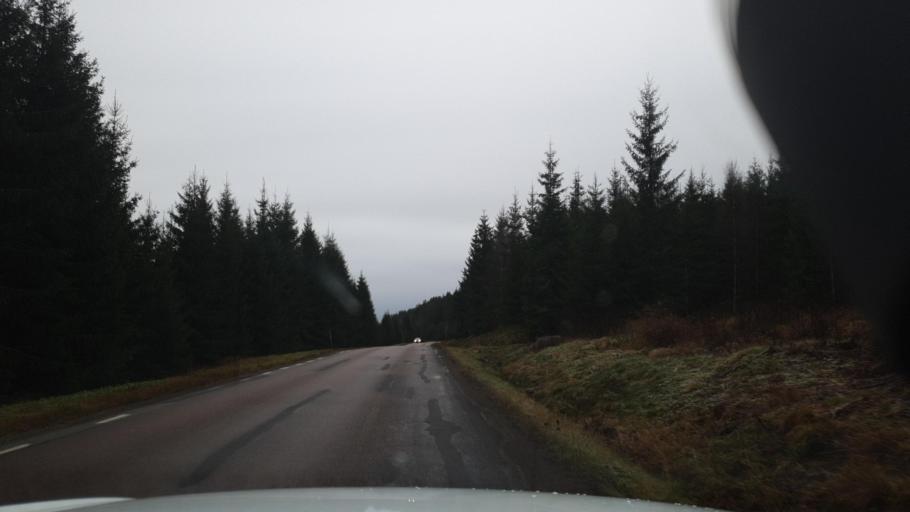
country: SE
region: Vaermland
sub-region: Arvika Kommun
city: Arvika
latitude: 59.7078
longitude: 12.7922
